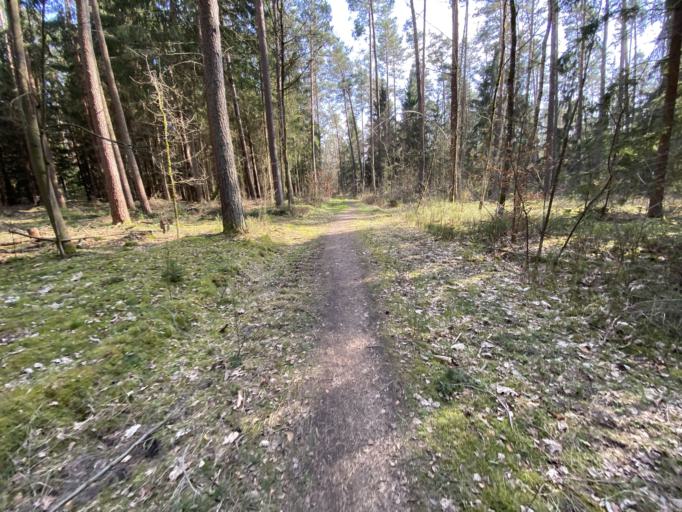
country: DE
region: Bavaria
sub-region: Regierungsbezirk Mittelfranken
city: Erlangen
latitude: 49.5617
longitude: 11.0266
